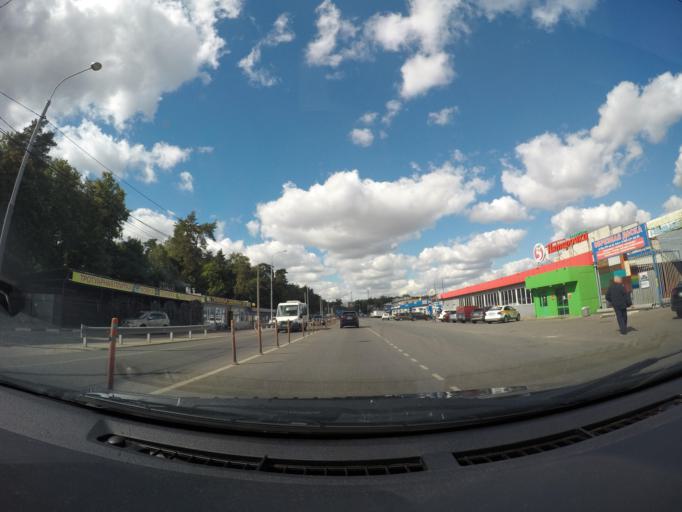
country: RU
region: Moskovskaya
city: Malakhovka
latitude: 55.6605
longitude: 38.0193
